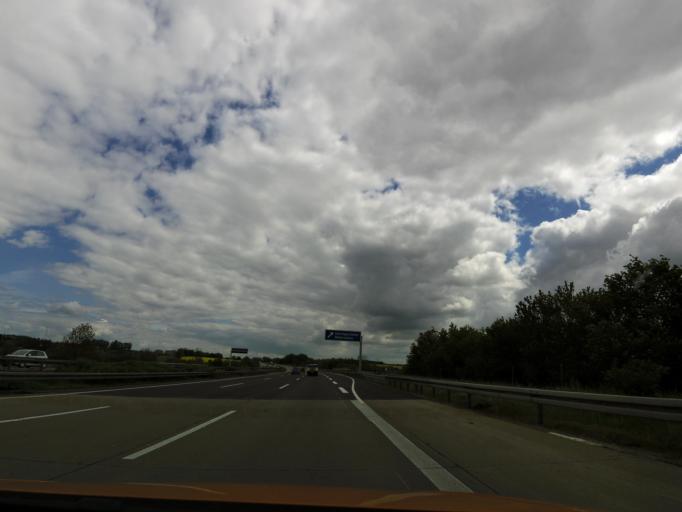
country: DE
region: Saxony-Anhalt
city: Wefensleben
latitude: 52.2072
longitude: 11.1320
